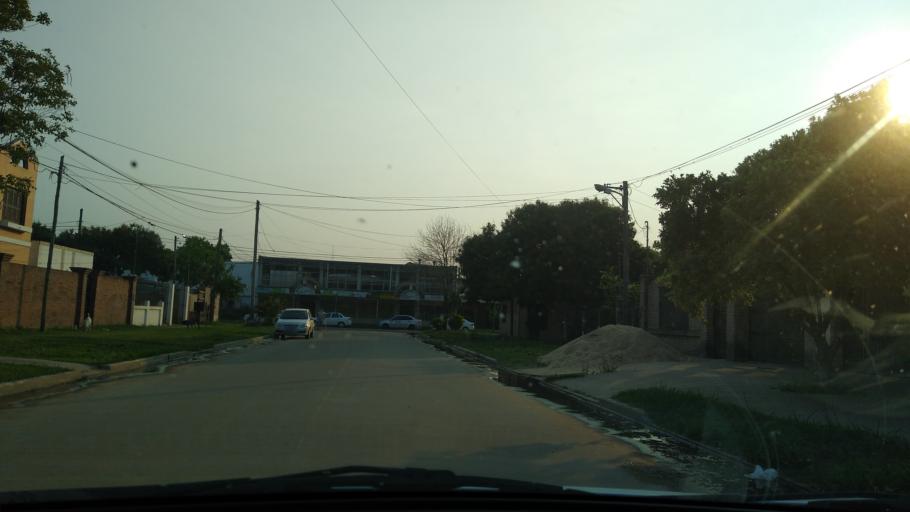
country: AR
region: Chaco
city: Barranqueras
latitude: -27.4839
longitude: -58.9407
